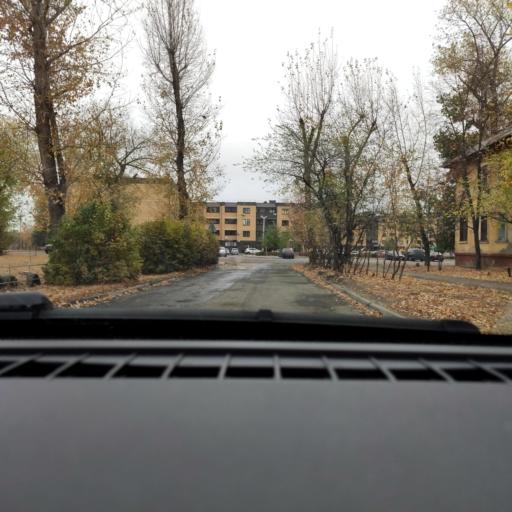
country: RU
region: Voronezj
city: Voronezh
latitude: 51.6643
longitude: 39.2777
